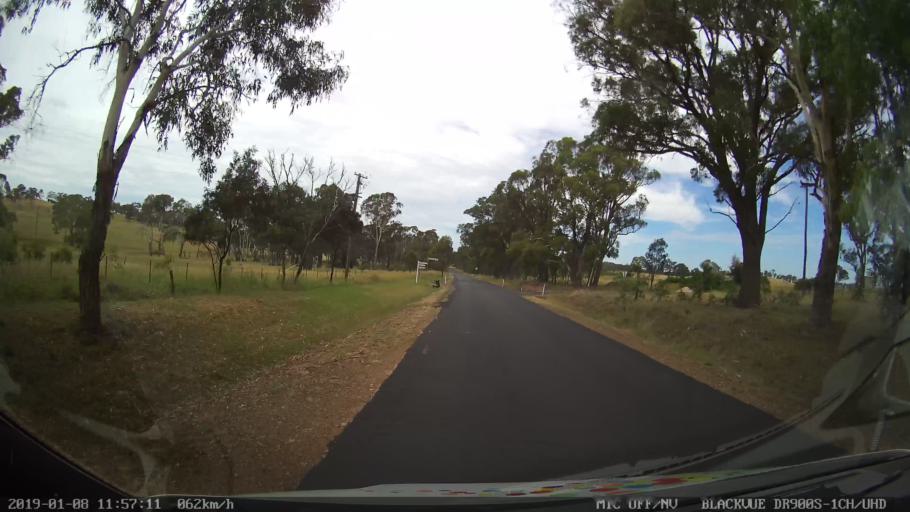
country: AU
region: New South Wales
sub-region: Armidale Dumaresq
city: Armidale
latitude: -30.4477
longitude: 151.5658
